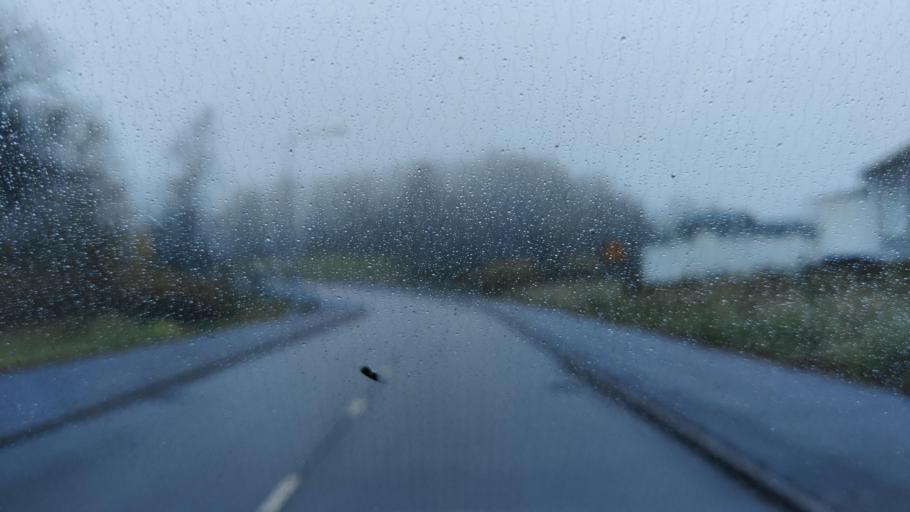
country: FI
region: Uusimaa
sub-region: Helsinki
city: Kerava
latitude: 60.3655
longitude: 25.0825
